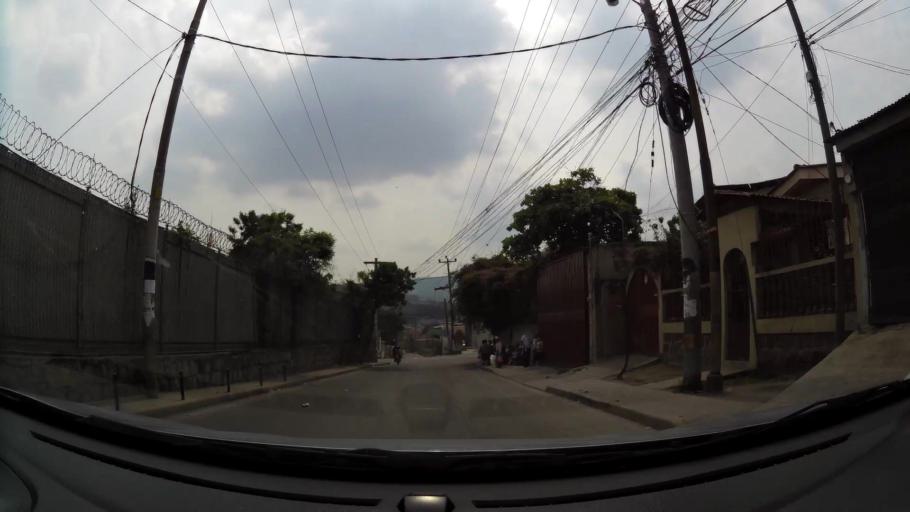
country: HN
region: Francisco Morazan
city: Tegucigalpa
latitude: 14.0927
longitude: -87.2226
